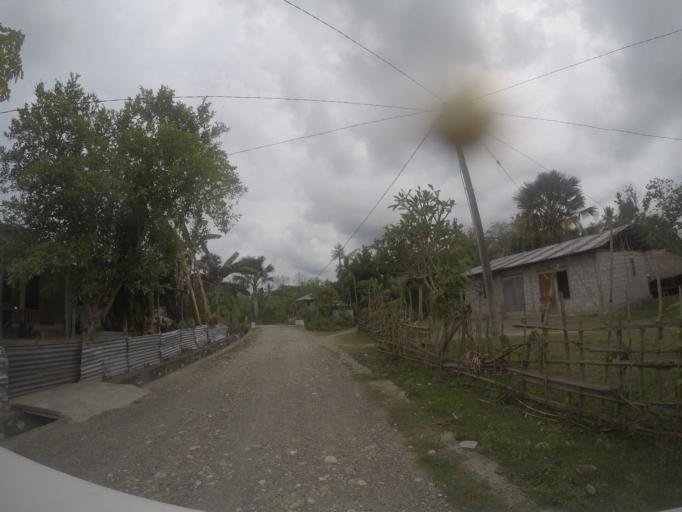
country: TL
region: Viqueque
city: Viqueque
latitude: -8.8794
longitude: 126.3664
